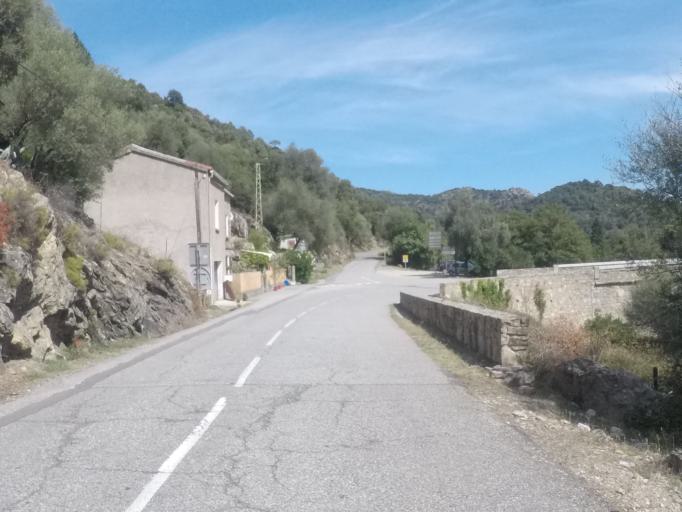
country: FR
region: Corsica
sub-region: Departement de la Haute-Corse
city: Corte
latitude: 42.3836
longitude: 9.1373
